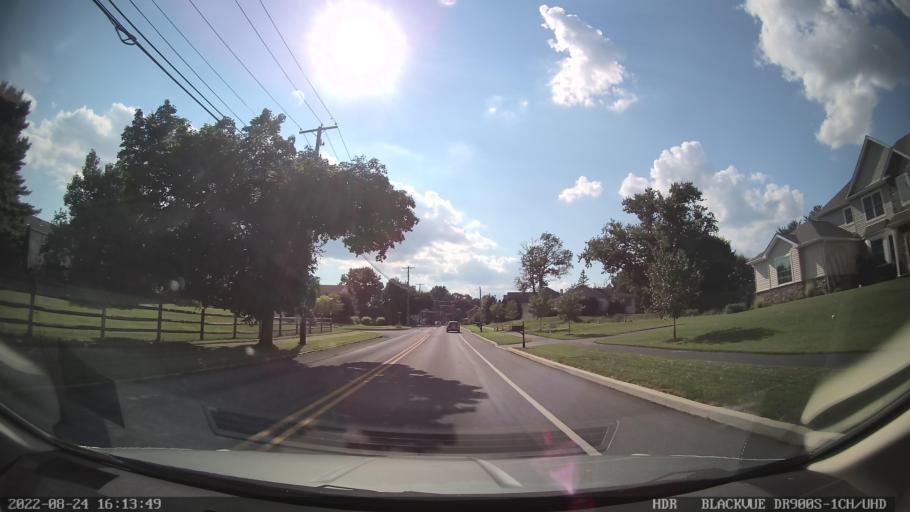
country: US
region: Pennsylvania
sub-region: Lehigh County
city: Wescosville
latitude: 40.5537
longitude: -75.5509
